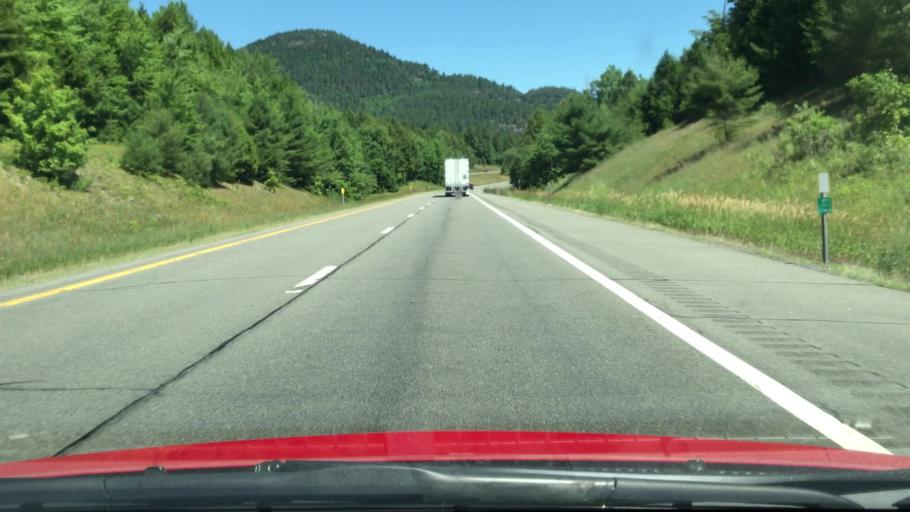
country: US
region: New York
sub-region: Essex County
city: Mineville
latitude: 43.9918
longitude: -73.7223
